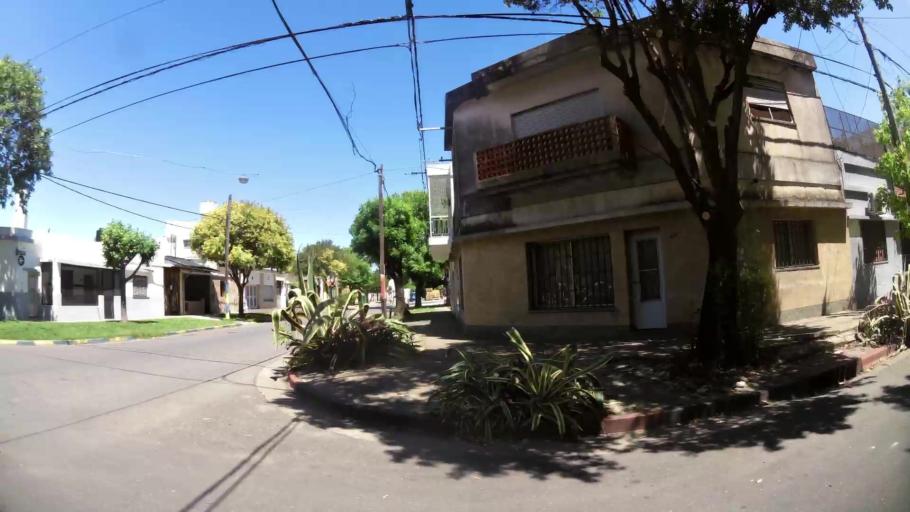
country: AR
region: Santa Fe
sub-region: Departamento de Rosario
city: Rosario
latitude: -32.9435
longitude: -60.7137
